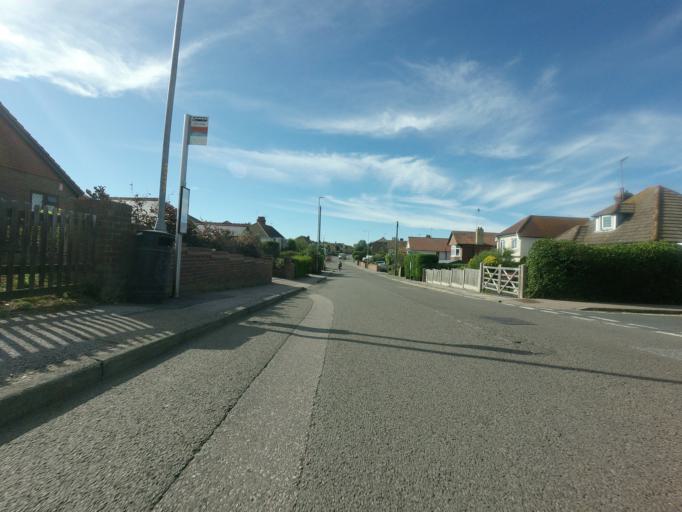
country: GB
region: England
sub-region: Kent
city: Herne Bay
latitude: 51.3705
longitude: 1.1618
